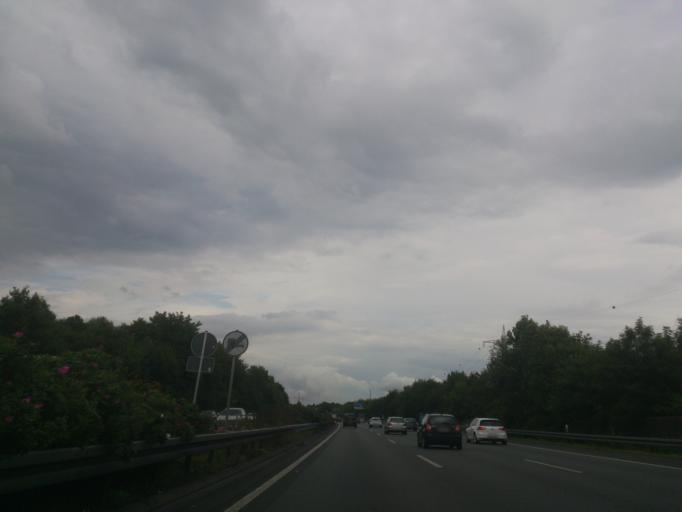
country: DE
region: North Rhine-Westphalia
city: Schwerte
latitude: 51.4641
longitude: 7.5851
